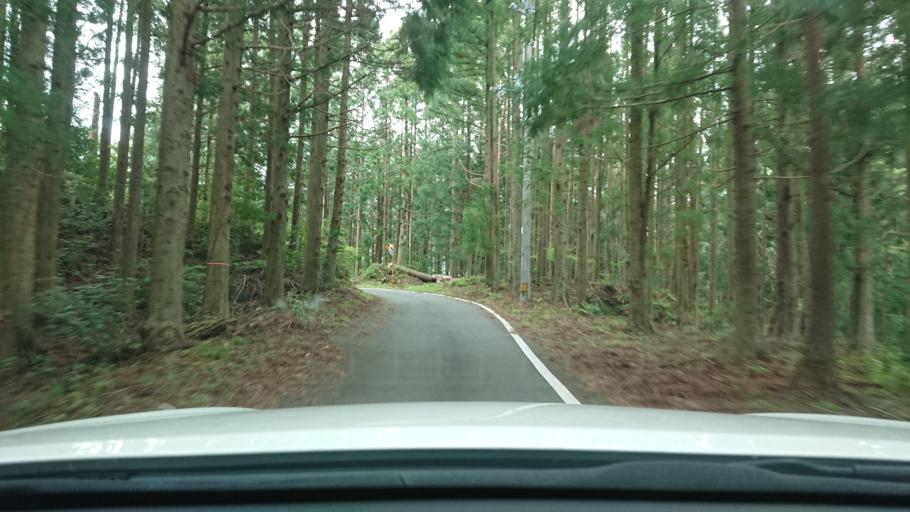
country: JP
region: Tokushima
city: Kamojimacho-jogejima
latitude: 33.8829
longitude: 134.3821
